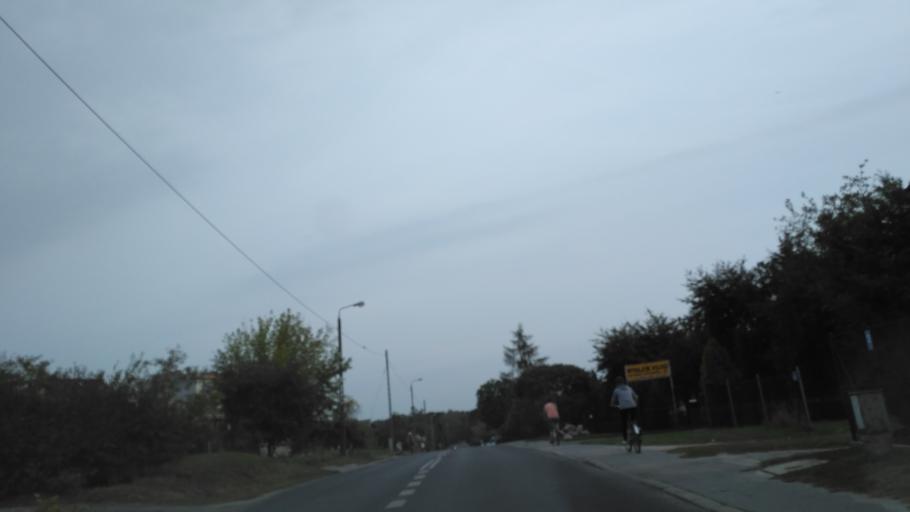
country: PL
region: Lublin Voivodeship
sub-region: Powiat lubelski
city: Lublin
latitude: 51.2128
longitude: 22.5931
